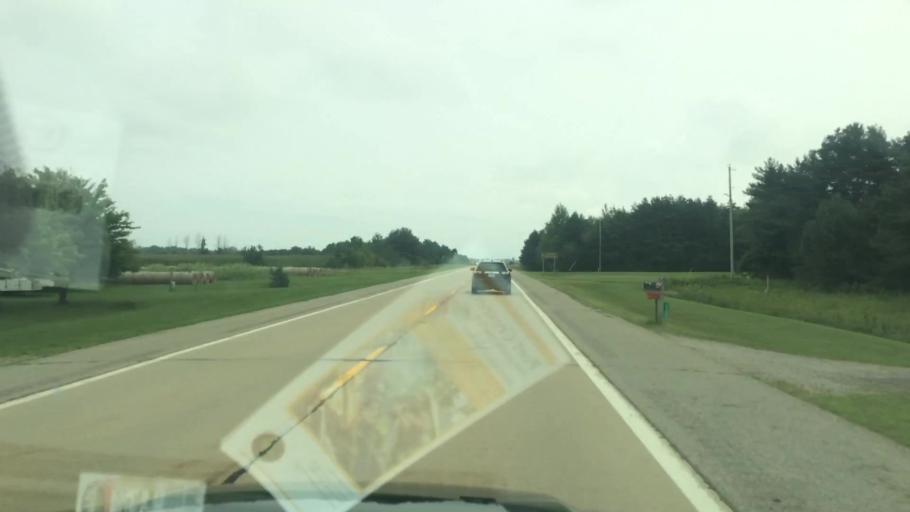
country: US
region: Michigan
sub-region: Huron County
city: Bad Axe
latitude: 44.0431
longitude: -82.9230
